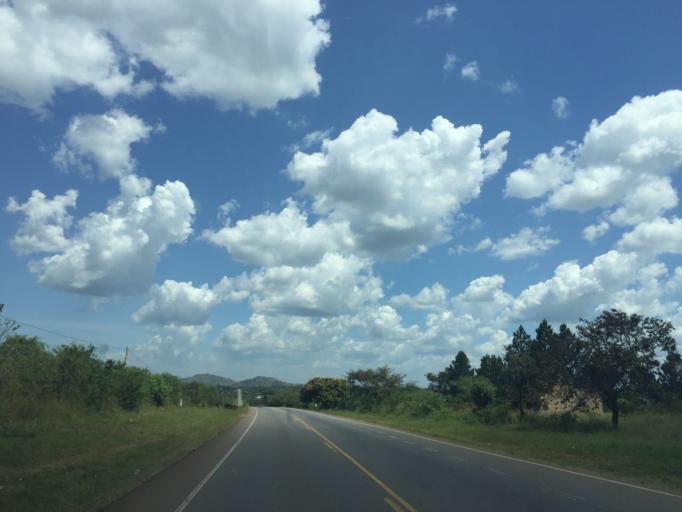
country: UG
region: Central Region
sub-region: Nakasongola District
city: Nakasongola
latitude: 1.3408
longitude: 32.3974
